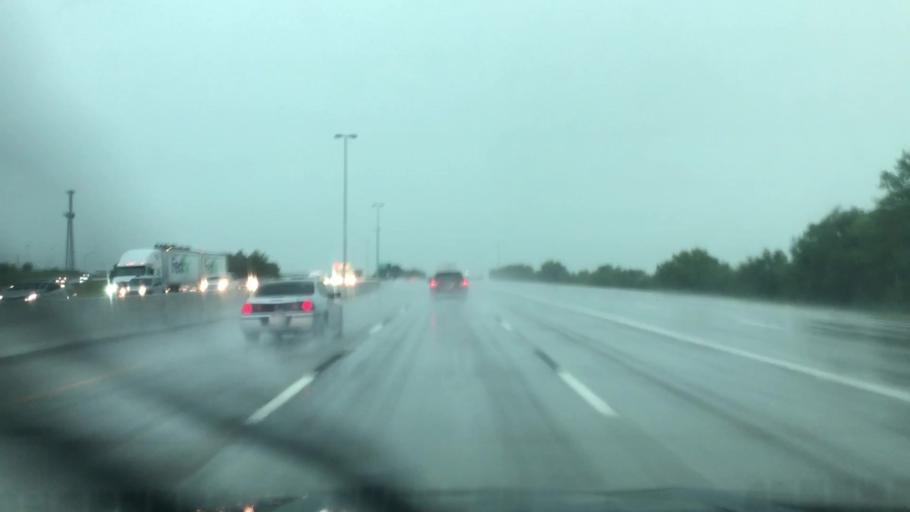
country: US
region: Oklahoma
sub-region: Rogers County
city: Catoosa
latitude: 36.1627
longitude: -95.8195
